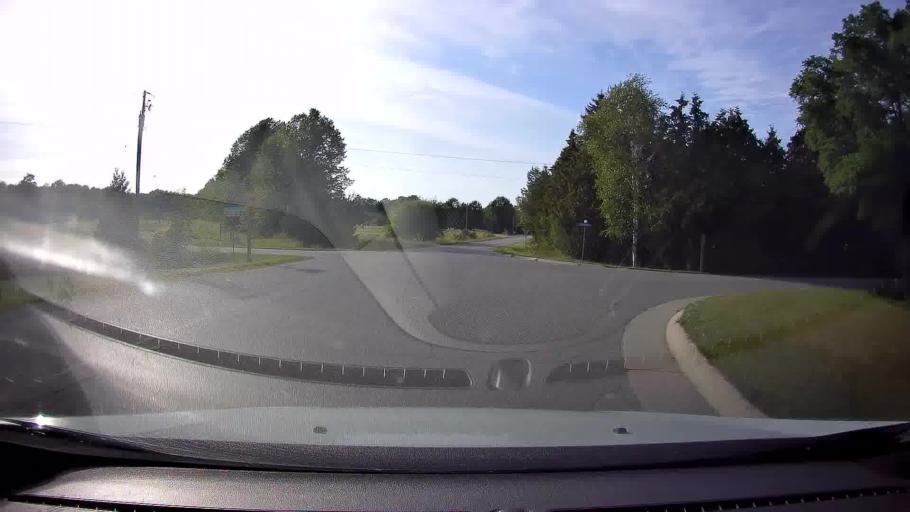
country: US
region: Wisconsin
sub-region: Door County
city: Sturgeon Bay
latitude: 45.1708
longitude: -87.1324
